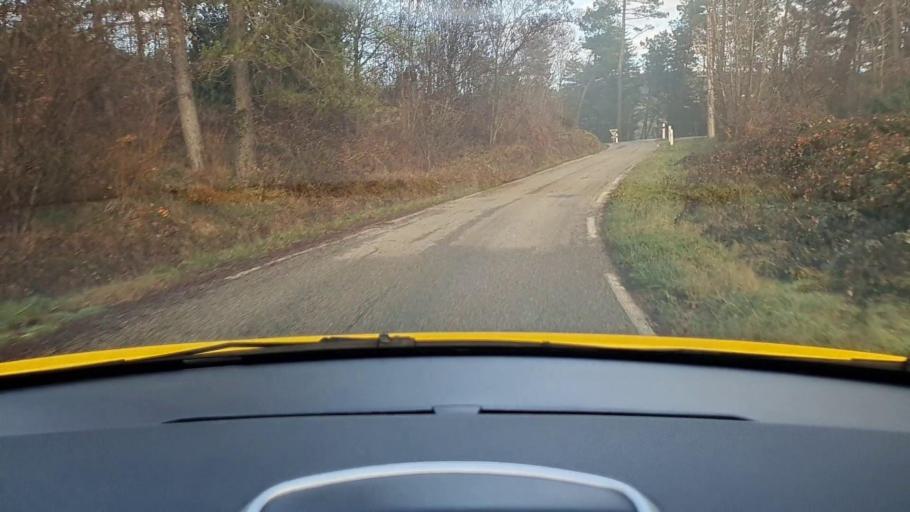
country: FR
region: Languedoc-Roussillon
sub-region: Departement du Gard
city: Branoux-les-Taillades
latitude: 44.2961
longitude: 4.0044
